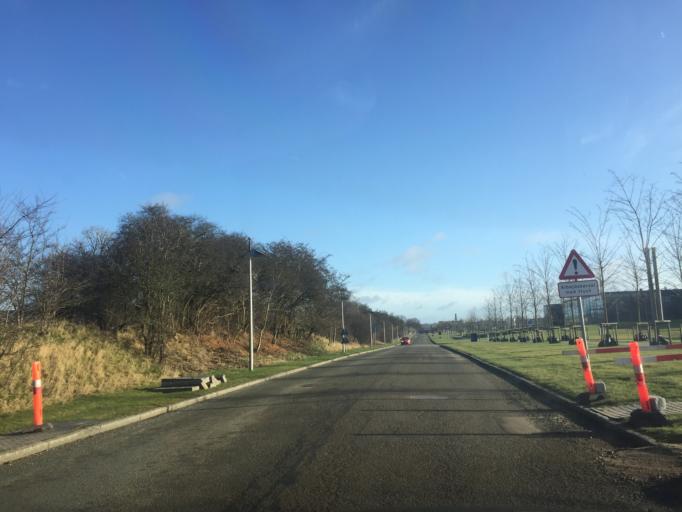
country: DK
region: Capital Region
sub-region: Hillerod Kommune
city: Hillerod
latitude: 55.9154
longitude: 12.2738
